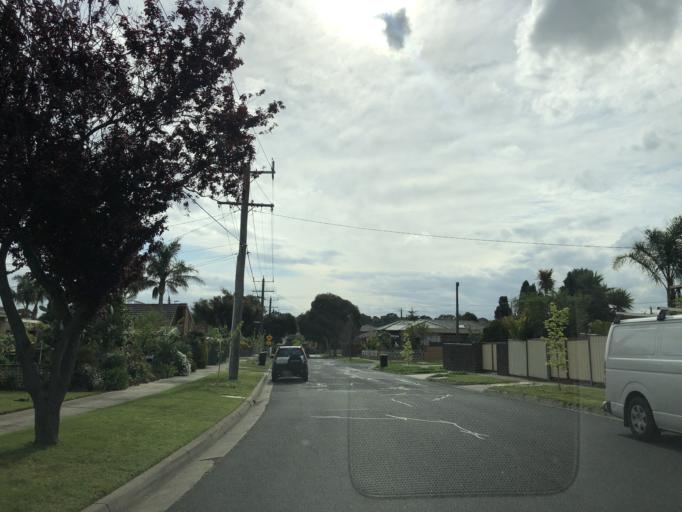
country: AU
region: Victoria
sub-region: Greater Dandenong
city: Noble Park North
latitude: -37.9461
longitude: 145.1948
